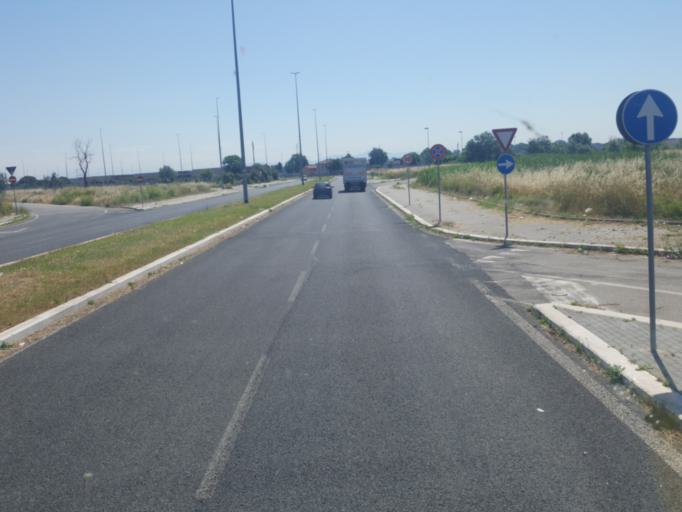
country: IT
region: Latium
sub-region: Citta metropolitana di Roma Capitale
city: Npp 23 (Parco Leonardo)
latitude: 41.8018
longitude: 12.3170
